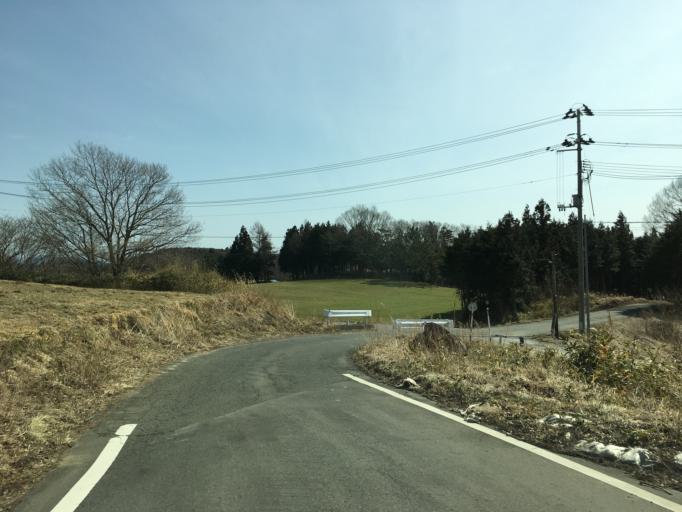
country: JP
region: Fukushima
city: Nihommatsu
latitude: 37.6282
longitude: 140.3606
